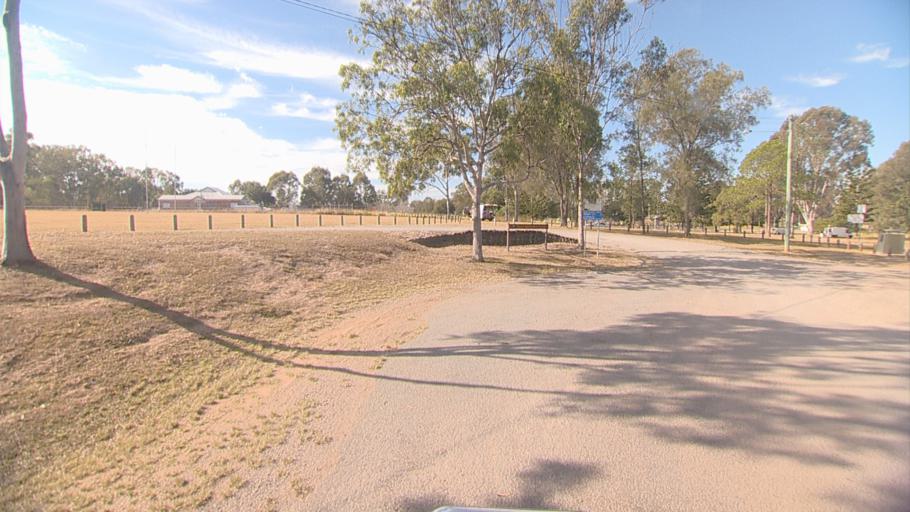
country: AU
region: Queensland
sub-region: Logan
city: North Maclean
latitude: -27.7825
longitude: 153.0094
